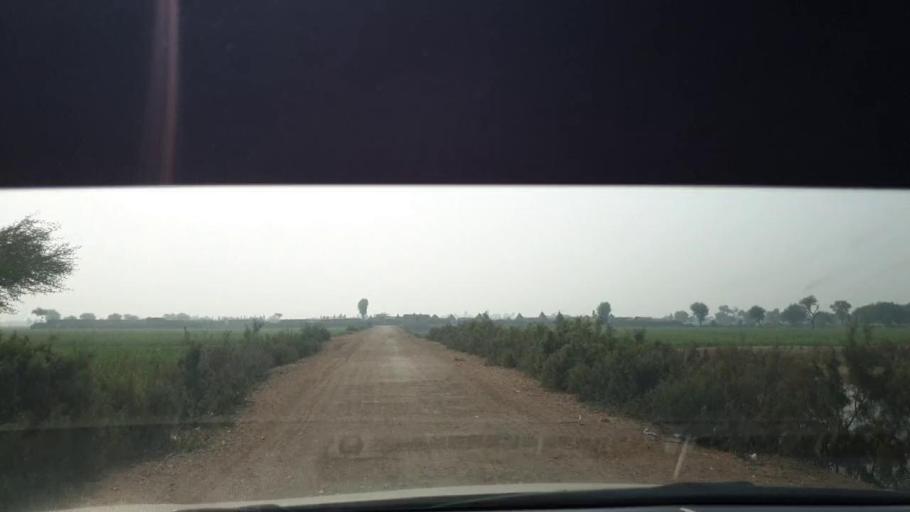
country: PK
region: Sindh
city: Berani
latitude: 25.7726
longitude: 68.8007
